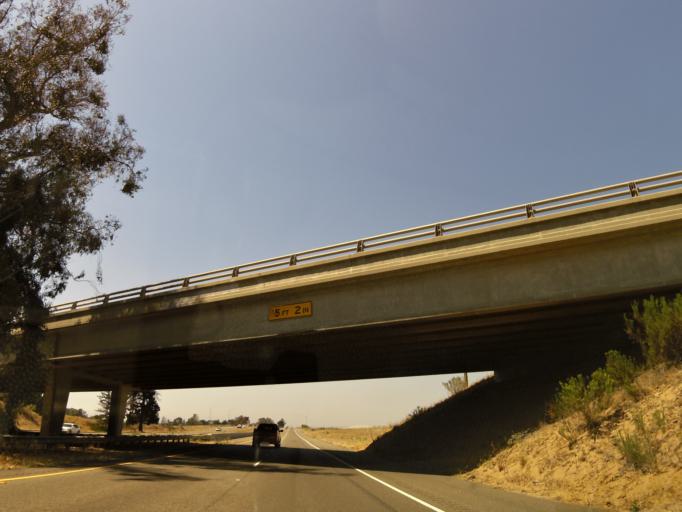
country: US
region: California
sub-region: Santa Barbara County
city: Orcutt
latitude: 34.8651
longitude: -120.3957
